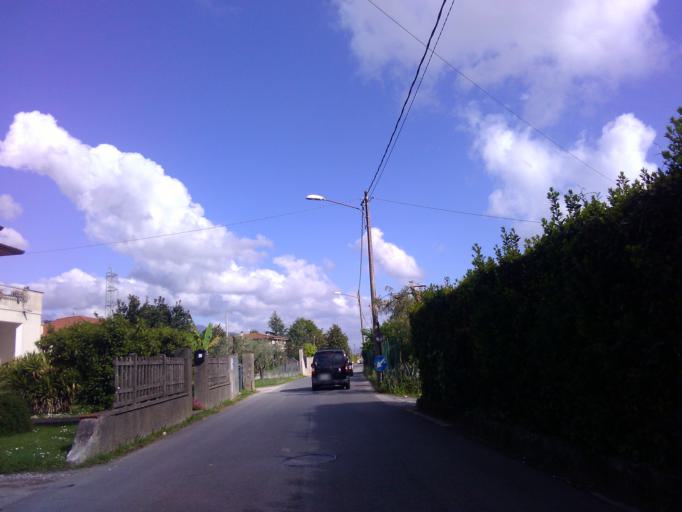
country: IT
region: Tuscany
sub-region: Provincia di Massa-Carrara
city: Massa
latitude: 44.0127
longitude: 10.1365
